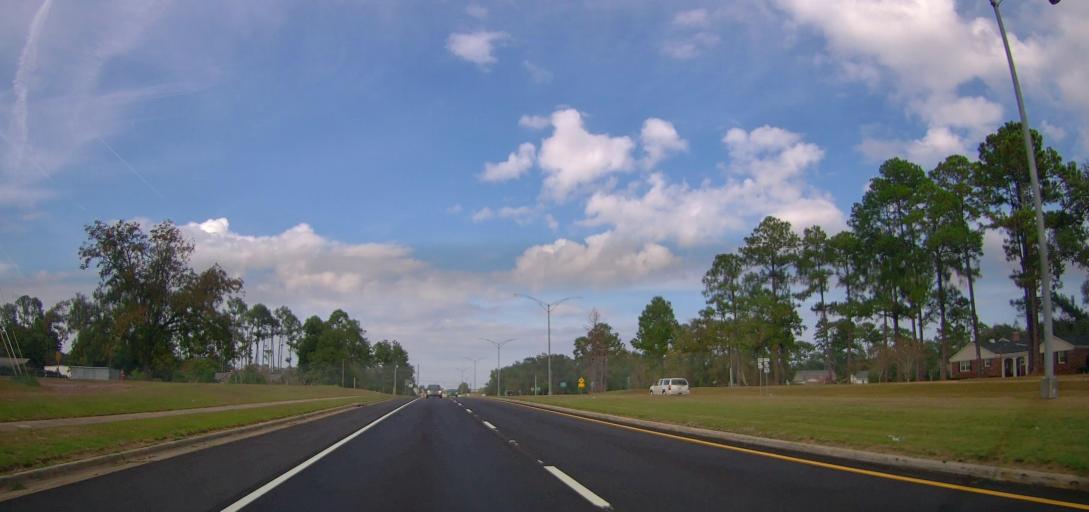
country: US
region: Georgia
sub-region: Mitchell County
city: Pelham
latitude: 31.1285
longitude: -84.1404
